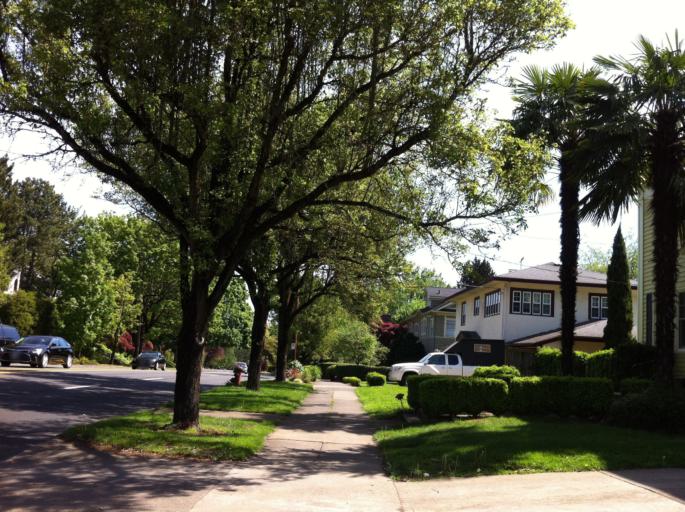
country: US
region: Oregon
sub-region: Multnomah County
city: Portland
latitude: 45.5228
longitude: -122.6273
